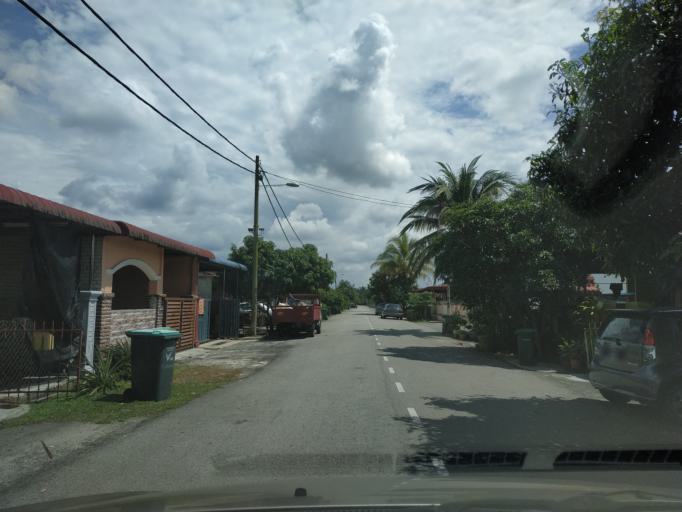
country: MY
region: Perak
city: Parit Buntar
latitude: 5.1398
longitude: 100.5950
